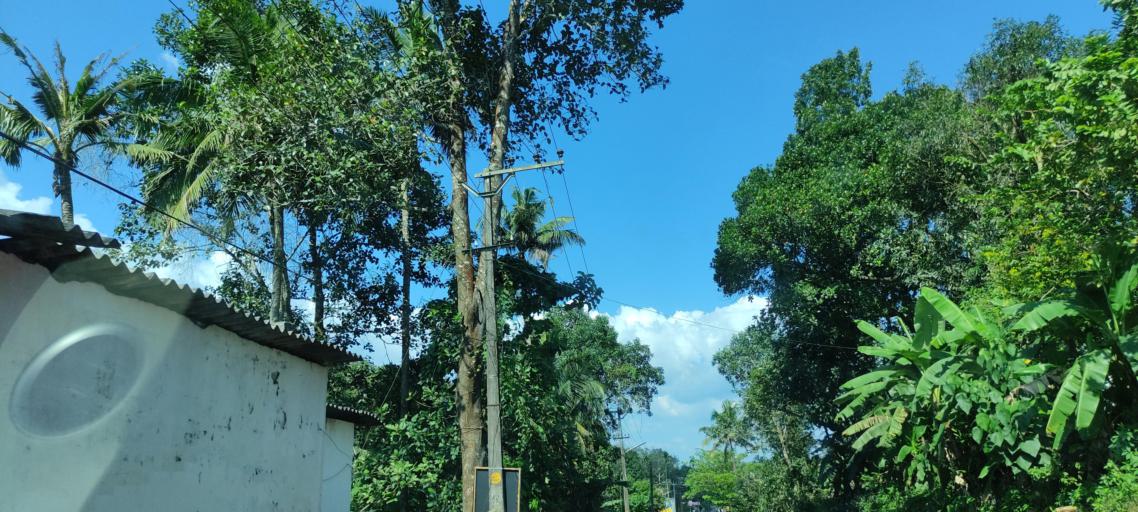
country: IN
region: Kerala
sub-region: Pattanamtitta
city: Adur
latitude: 9.1795
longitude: 76.7426
